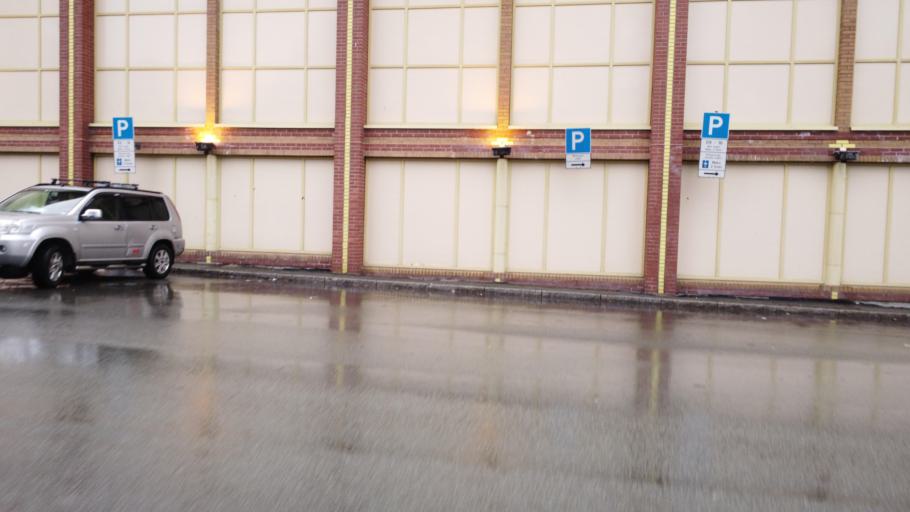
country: NO
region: Nordland
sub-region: Rana
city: Mo i Rana
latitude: 66.3113
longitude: 14.1356
